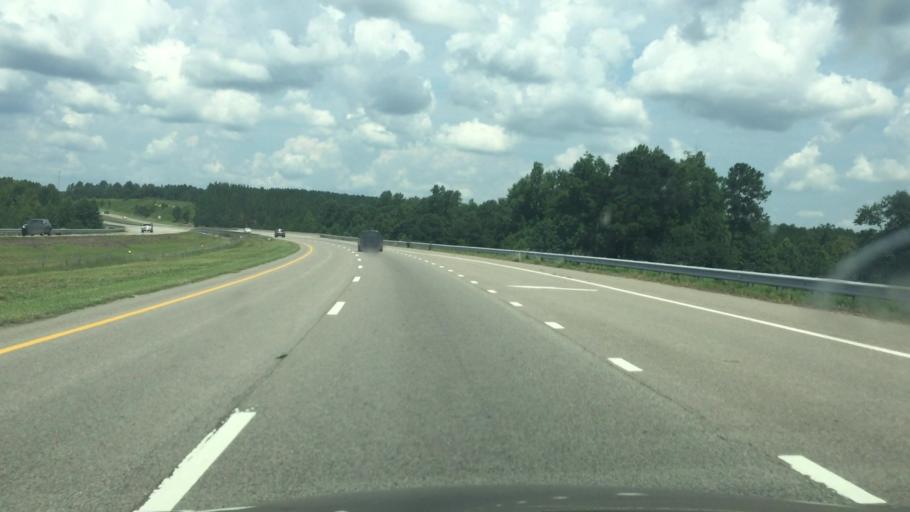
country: US
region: North Carolina
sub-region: Richmond County
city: Ellerbe
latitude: 35.1792
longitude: -79.7134
